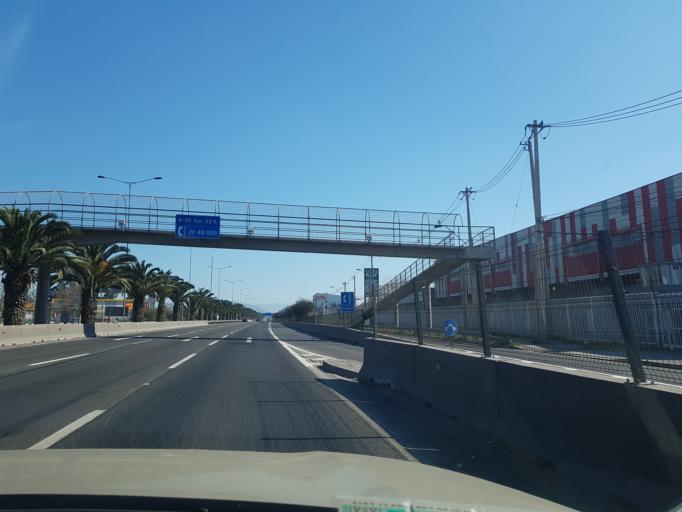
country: CL
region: Santiago Metropolitan
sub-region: Provincia de Santiago
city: Lo Prado
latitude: -33.3790
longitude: -70.7515
